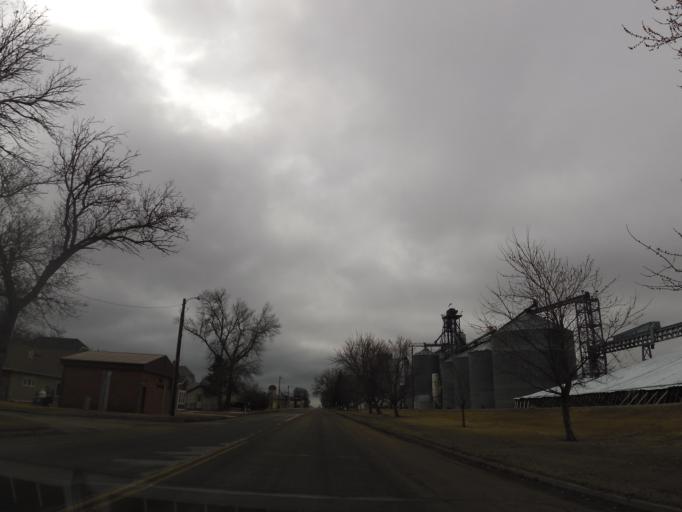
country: US
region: North Dakota
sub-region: Cass County
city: Casselton
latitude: 47.1055
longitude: -97.2181
